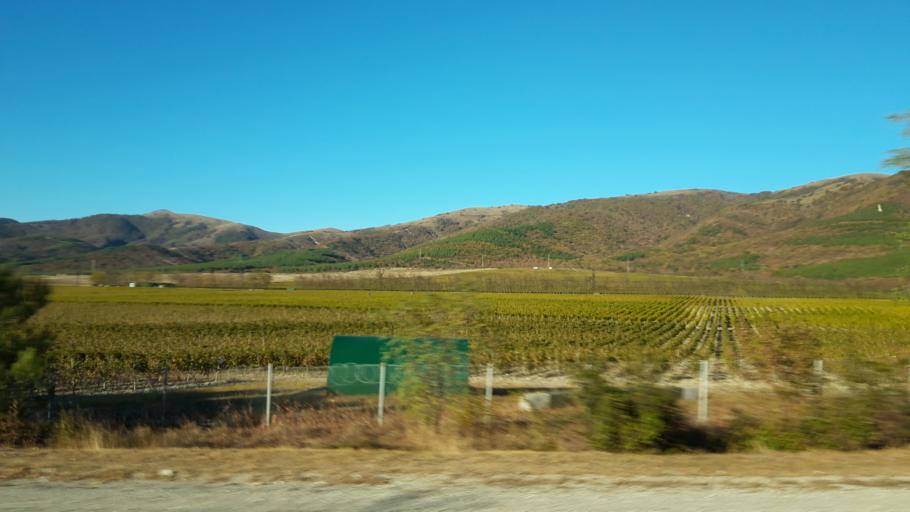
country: RU
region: Krasnodarskiy
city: Kabardinka
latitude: 44.6249
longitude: 38.0122
